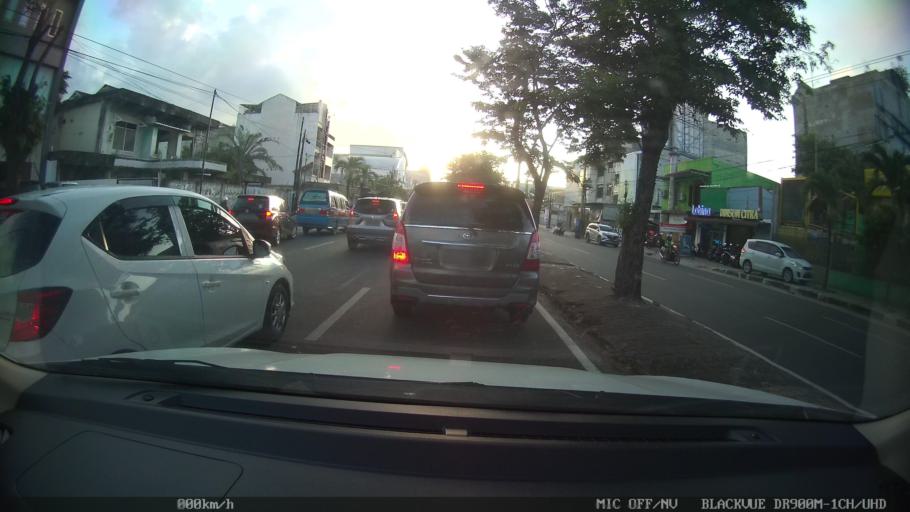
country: ID
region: North Sumatra
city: Medan
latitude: 3.5901
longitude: 98.6561
